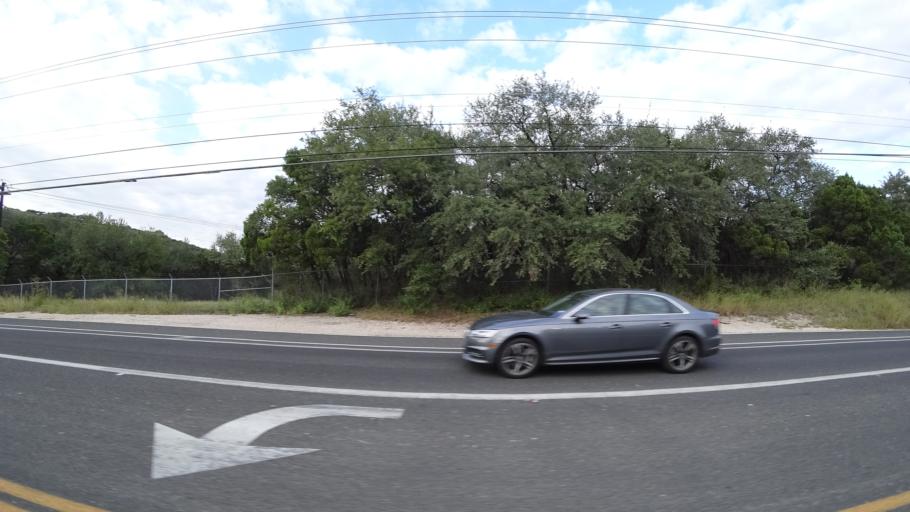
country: US
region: Texas
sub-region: Travis County
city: West Lake Hills
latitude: 30.2914
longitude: -97.7949
